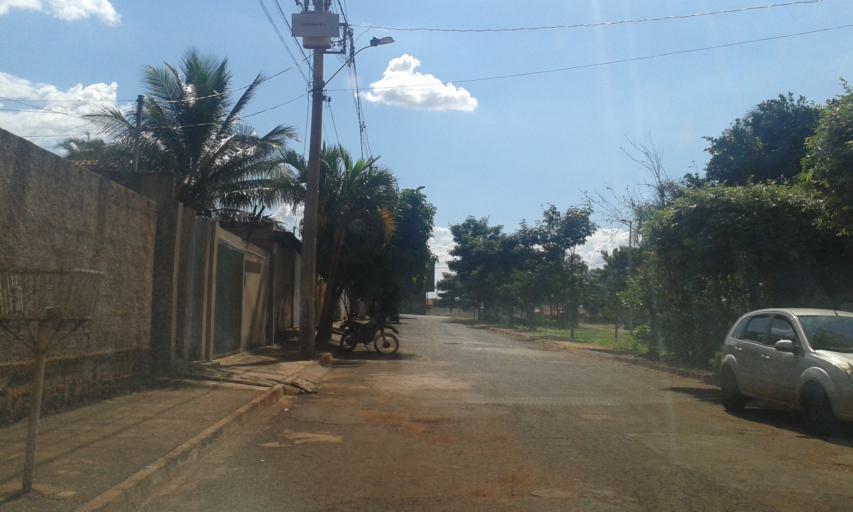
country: BR
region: Minas Gerais
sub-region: Capinopolis
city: Capinopolis
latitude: -18.6872
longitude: -49.5730
